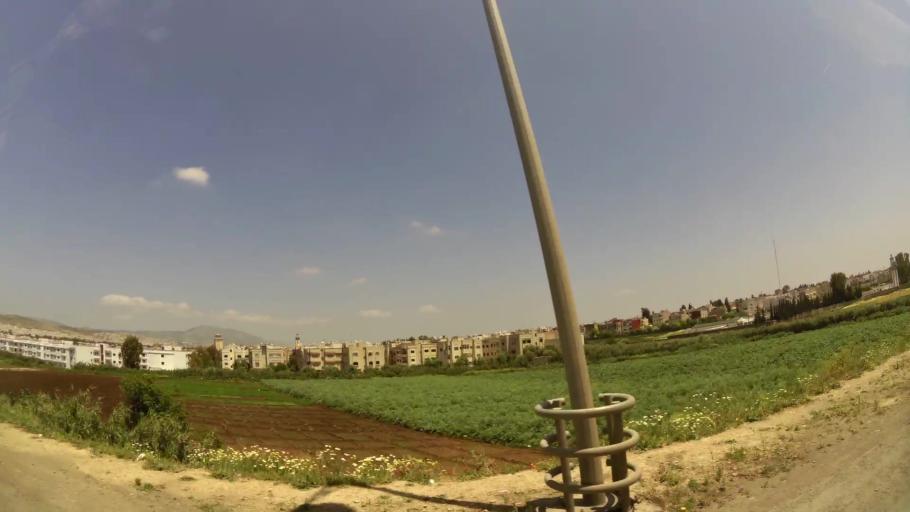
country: MA
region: Fes-Boulemane
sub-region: Fes
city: Fes
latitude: 34.0340
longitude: -5.0313
